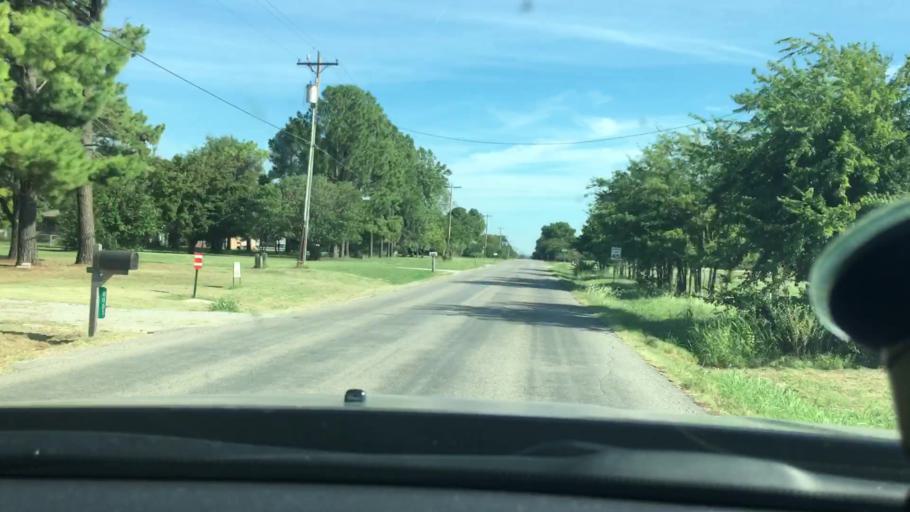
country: US
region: Oklahoma
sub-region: Carter County
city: Lone Grove
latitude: 34.2027
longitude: -97.2475
